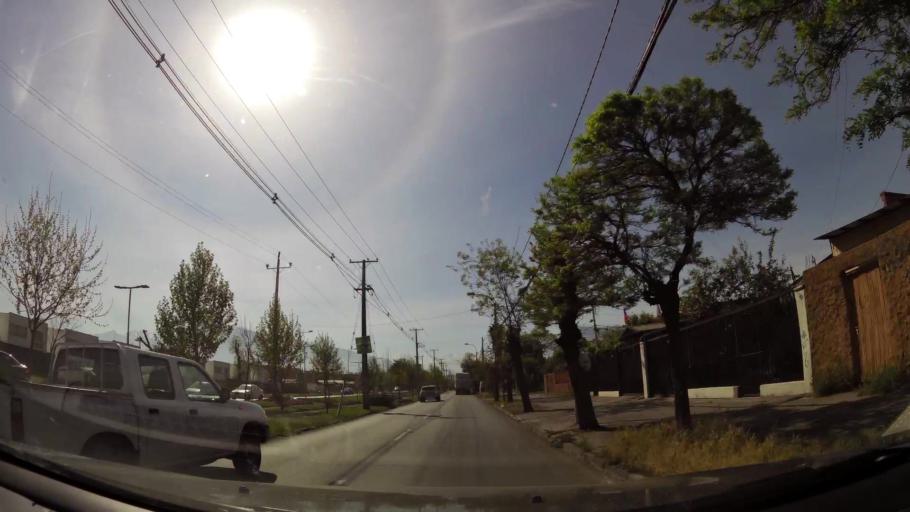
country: CL
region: Santiago Metropolitan
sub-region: Provincia de Cordillera
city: Puente Alto
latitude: -33.6042
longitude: -70.5874
